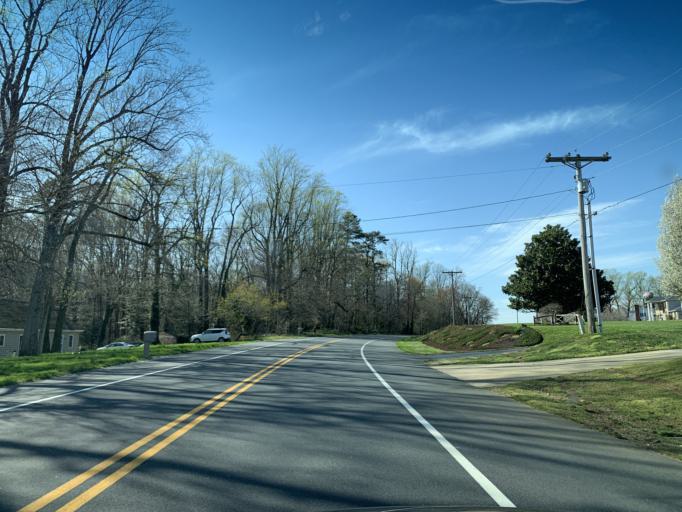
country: US
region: Delaware
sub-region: Kent County
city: Riverview
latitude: 38.9907
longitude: -75.5127
